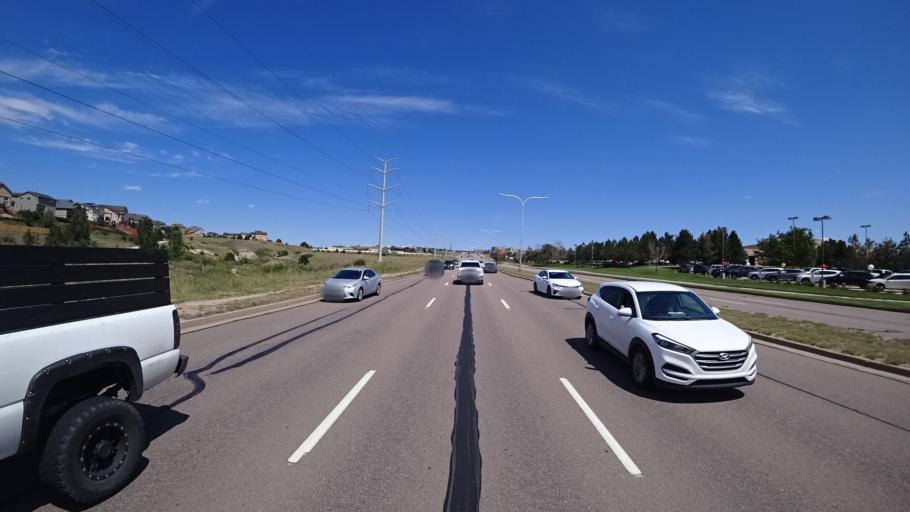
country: US
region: Colorado
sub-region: El Paso County
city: Black Forest
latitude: 38.9403
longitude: -104.7377
